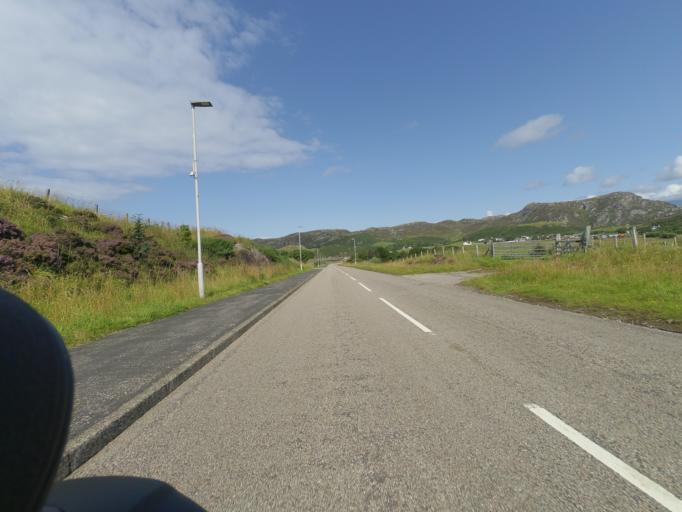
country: GB
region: Scotland
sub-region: Highland
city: Ullapool
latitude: 58.3473
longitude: -5.1611
